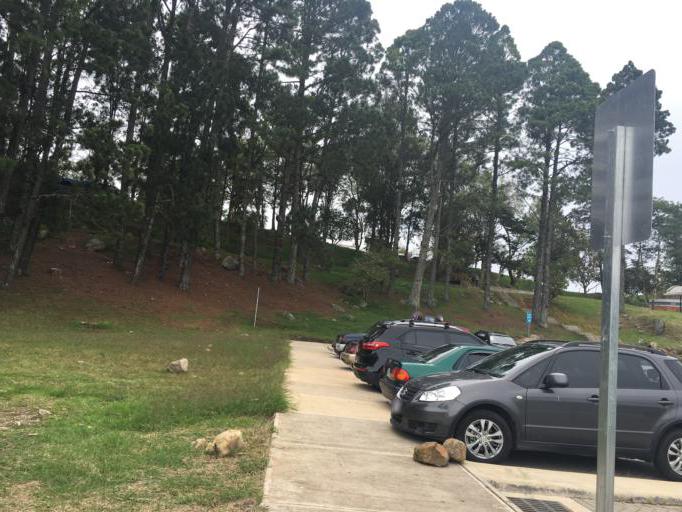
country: CR
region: Cartago
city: Cartago
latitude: 9.8568
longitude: -83.9110
